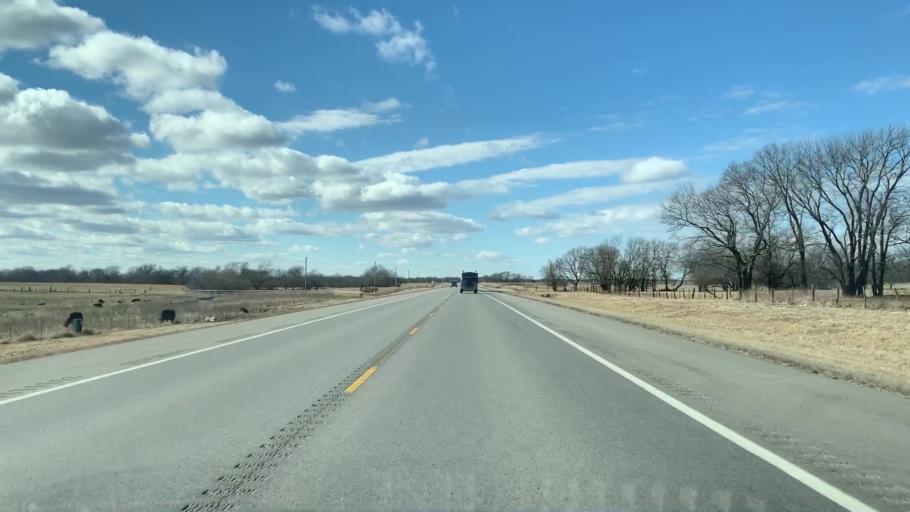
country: US
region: Kansas
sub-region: Crawford County
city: Pittsburg
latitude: 37.3397
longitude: -94.8570
